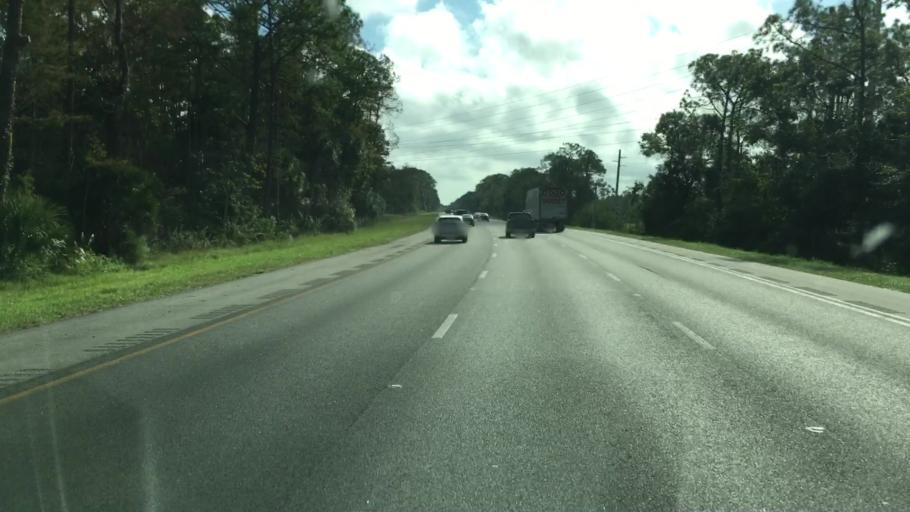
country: US
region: Florida
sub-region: Volusia County
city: Port Orange
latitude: 29.1294
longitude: -81.0598
